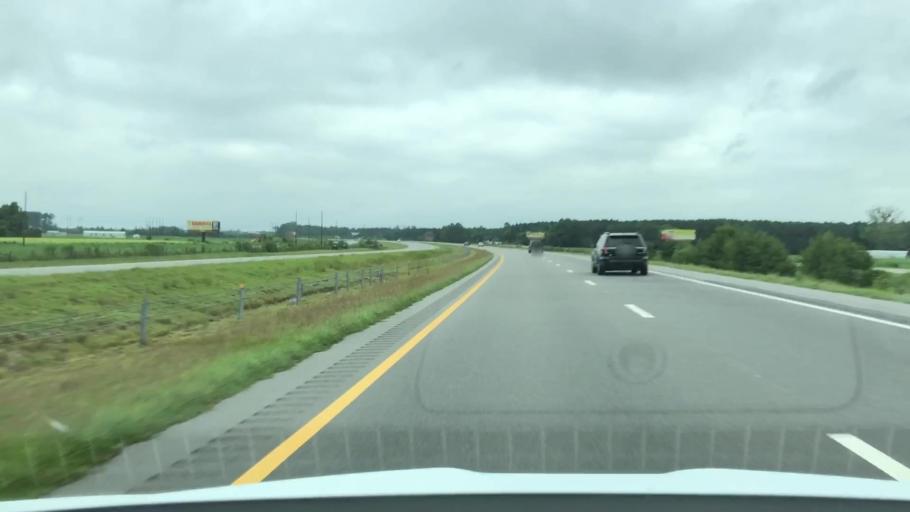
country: US
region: North Carolina
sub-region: Wayne County
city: Elroy
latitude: 35.3915
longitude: -77.8663
